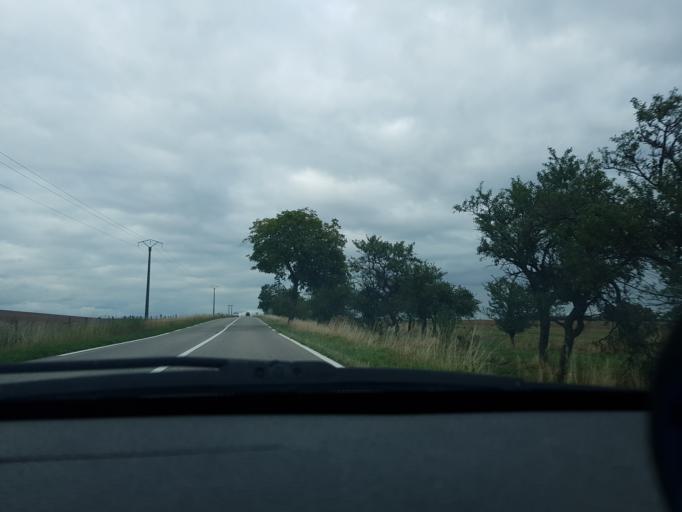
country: FR
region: Lorraine
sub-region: Departement de la Moselle
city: Chateau-Salins
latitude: 48.8643
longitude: 6.5272
